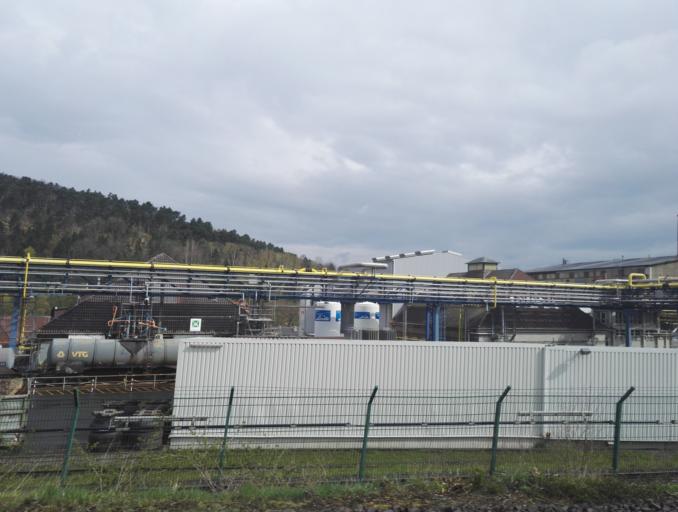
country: DE
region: Lower Saxony
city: Goslar
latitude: 51.9083
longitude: 10.4714
